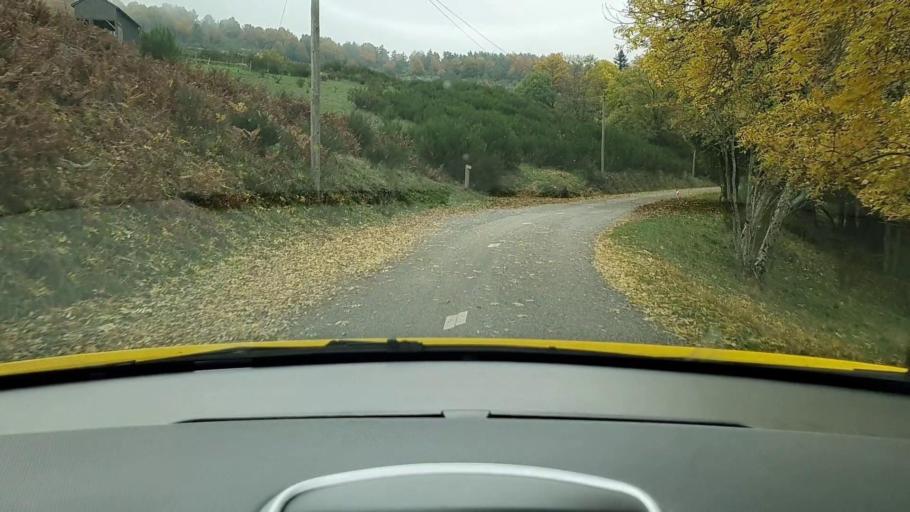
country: FR
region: Languedoc-Roussillon
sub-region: Departement du Gard
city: Le Vigan
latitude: 44.0730
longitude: 3.5175
